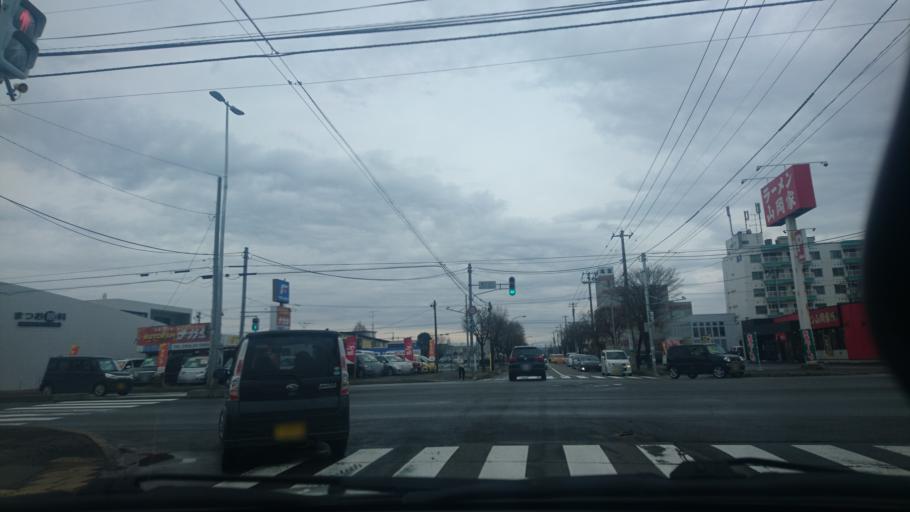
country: JP
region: Hokkaido
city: Obihiro
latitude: 42.9311
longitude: 143.1929
